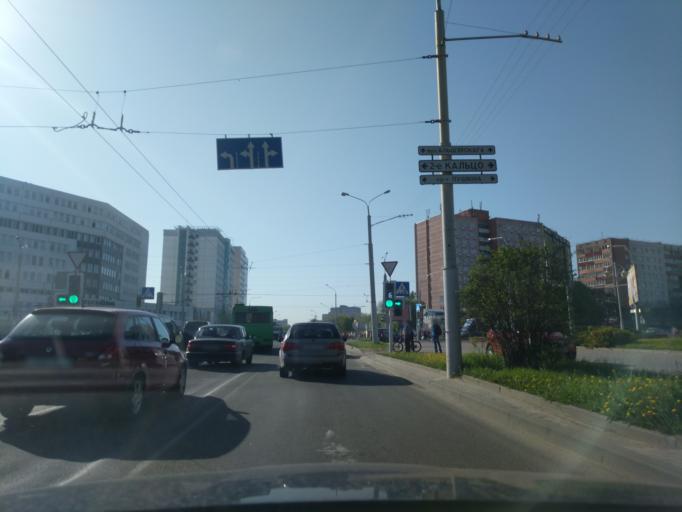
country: BY
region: Minsk
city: Novoye Medvezhino
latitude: 53.9207
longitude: 27.4978
